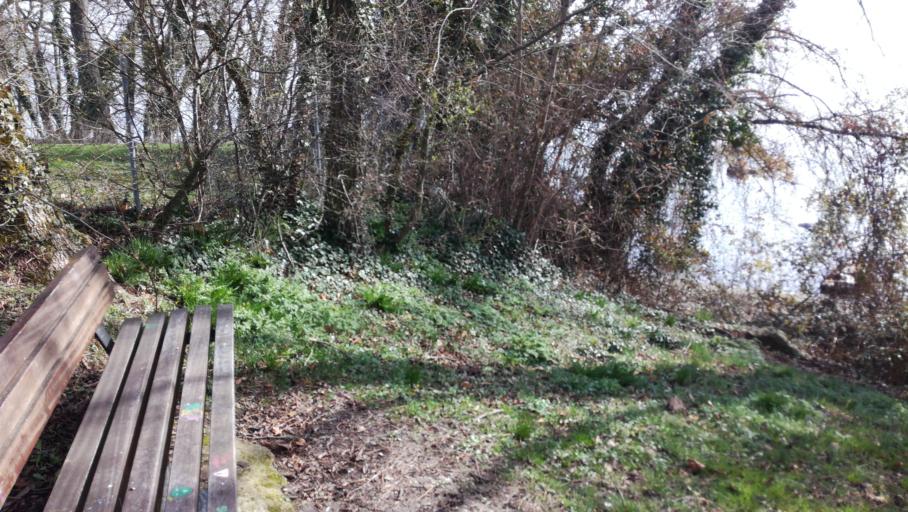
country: CH
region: Vaud
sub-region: Nyon District
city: Rolle
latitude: 46.4353
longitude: 6.3126
